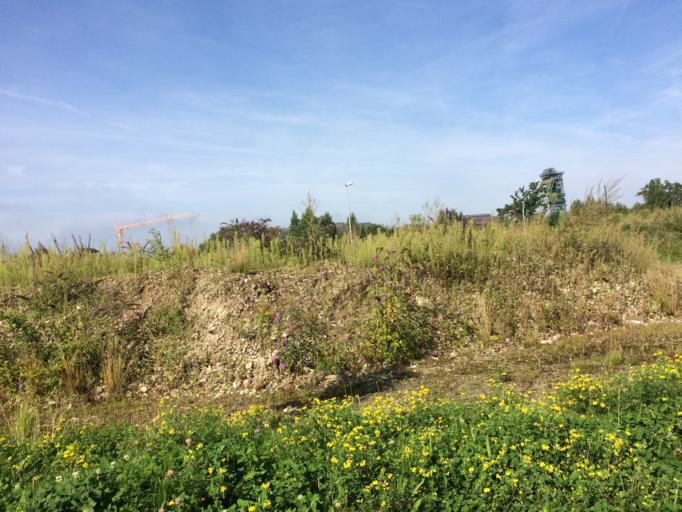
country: DE
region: North Rhine-Westphalia
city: Dorsten
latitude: 51.6723
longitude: 6.9878
